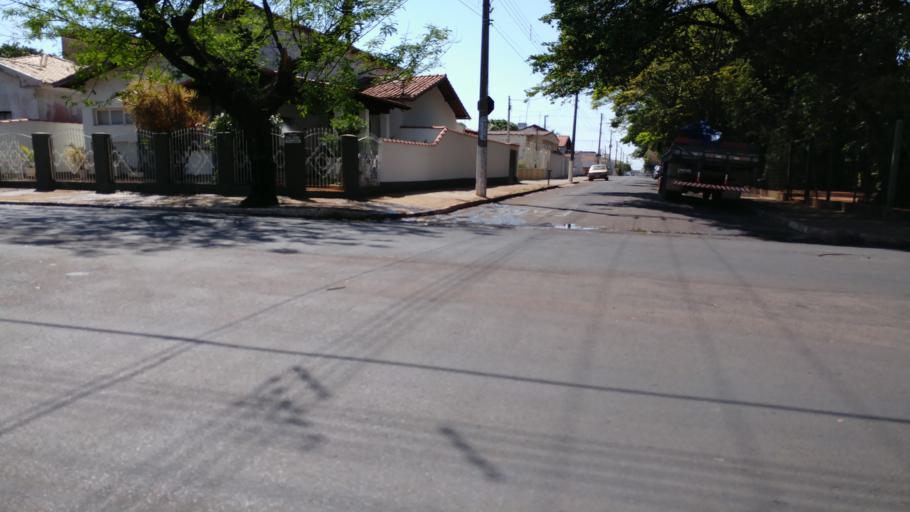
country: BR
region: Sao Paulo
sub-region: Paraguacu Paulista
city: Paraguacu Paulista
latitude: -22.4131
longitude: -50.5835
